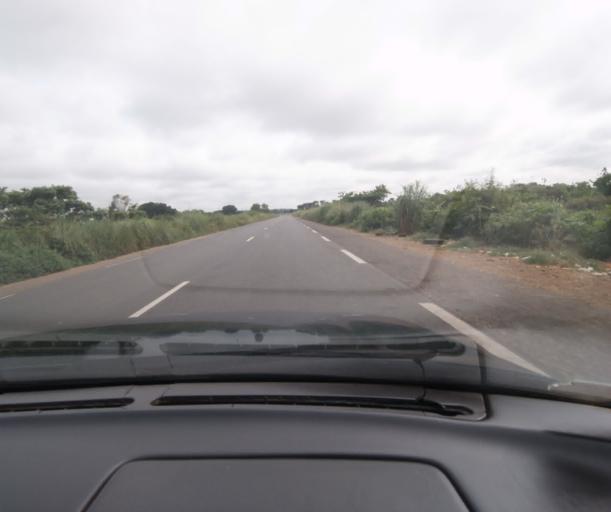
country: CM
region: Centre
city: Saa
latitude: 4.3832
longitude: 11.2560
